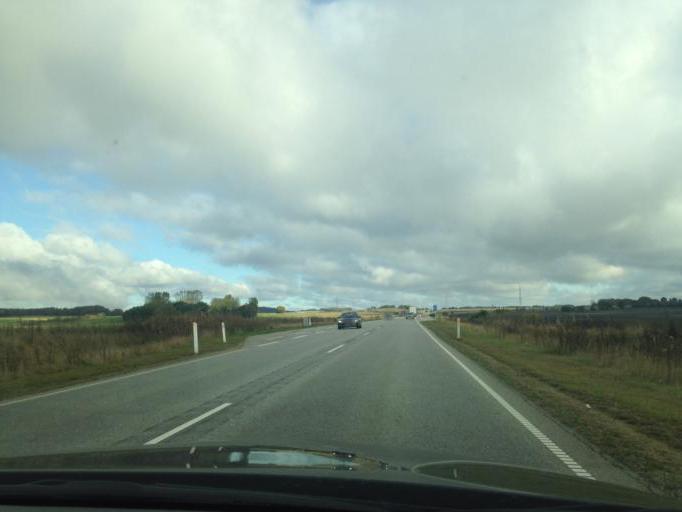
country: DK
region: South Denmark
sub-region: Vejle Kommune
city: Give
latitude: 55.8351
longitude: 9.2651
